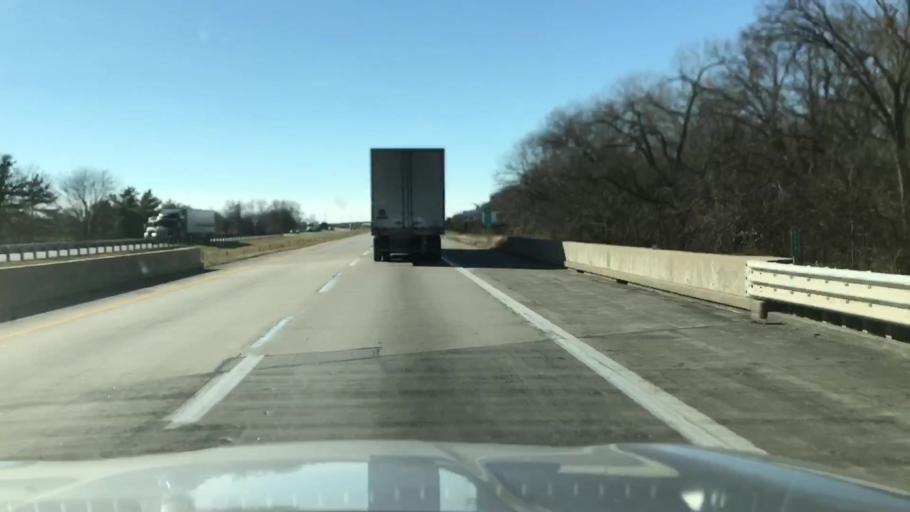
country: US
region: Missouri
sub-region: Jasper County
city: Duenweg
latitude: 37.0727
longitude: -94.3945
